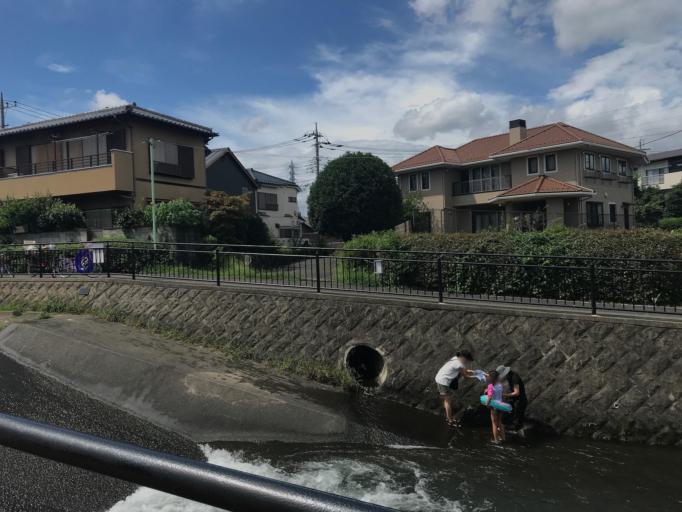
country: JP
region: Tokyo
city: Tanashicho
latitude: 35.7568
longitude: 139.5352
